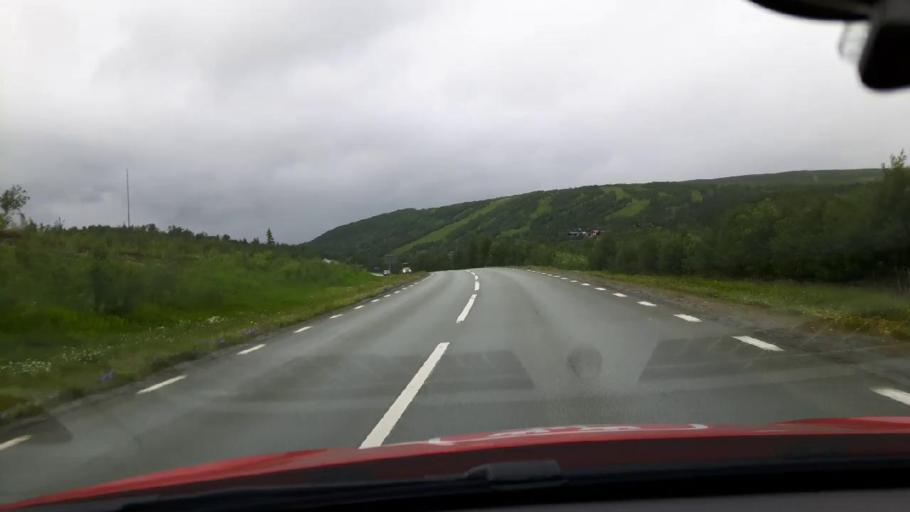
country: NO
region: Nord-Trondelag
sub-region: Meraker
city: Meraker
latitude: 63.3116
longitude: 12.1053
